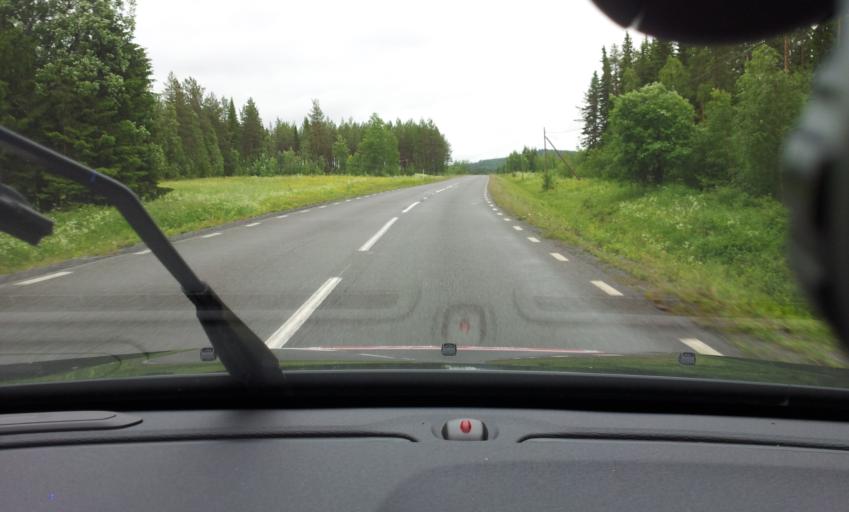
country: SE
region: Jaemtland
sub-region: OEstersunds Kommun
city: Lit
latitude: 63.6919
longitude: 15.0093
